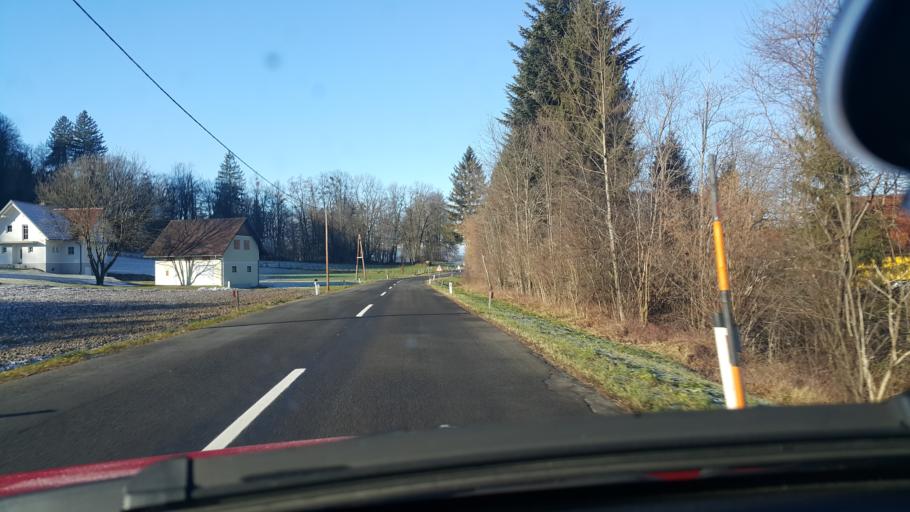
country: AT
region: Styria
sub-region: Politischer Bezirk Leibnitz
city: Leutschach
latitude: 46.6591
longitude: 15.4795
